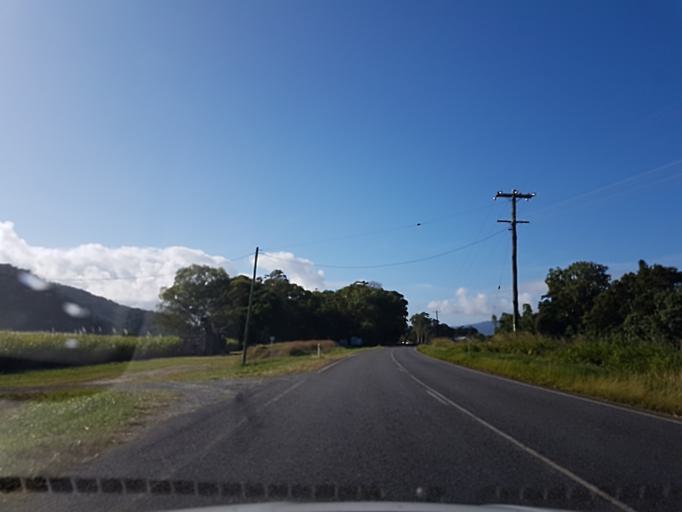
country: AU
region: Queensland
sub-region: Cairns
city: Port Douglas
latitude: -16.3417
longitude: 145.4091
